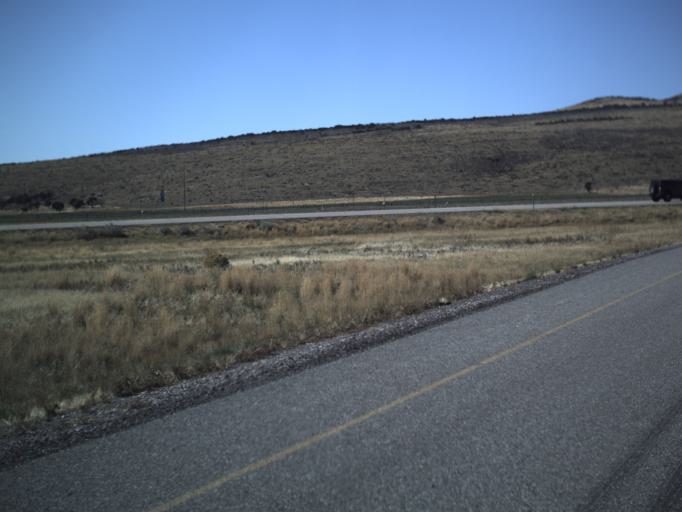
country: US
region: Utah
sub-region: Beaver County
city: Beaver
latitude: 38.5388
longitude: -112.6079
